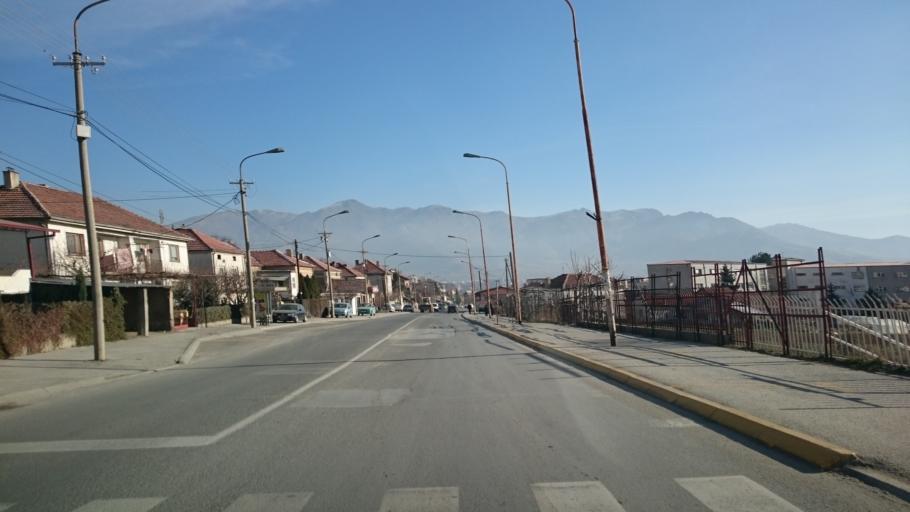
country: MK
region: Prilep
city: Markov Grad
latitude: 41.3542
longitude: 21.5418
